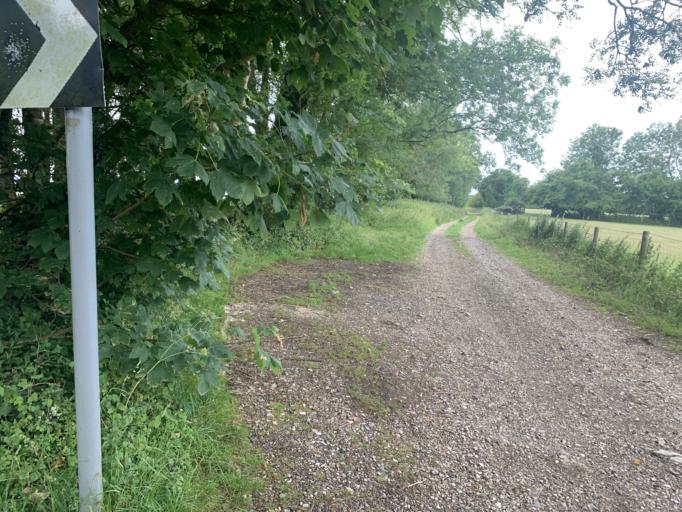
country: GB
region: England
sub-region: Wiltshire
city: Bower Chalke
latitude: 50.9939
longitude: -2.0143
